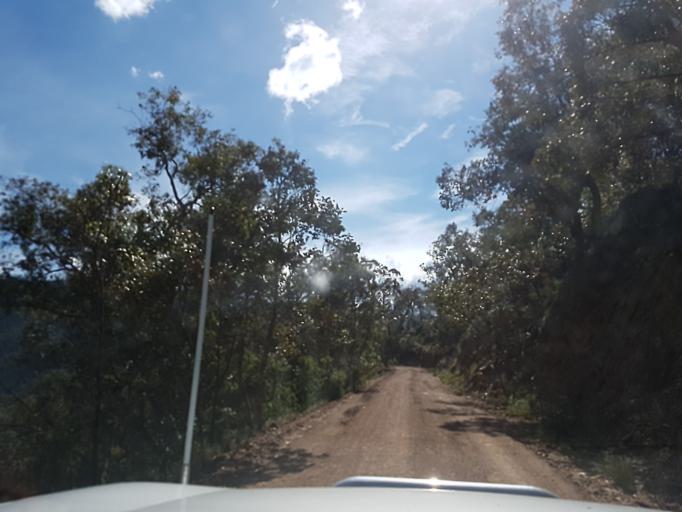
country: AU
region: Victoria
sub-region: Alpine
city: Mount Beauty
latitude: -37.3755
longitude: 147.0411
